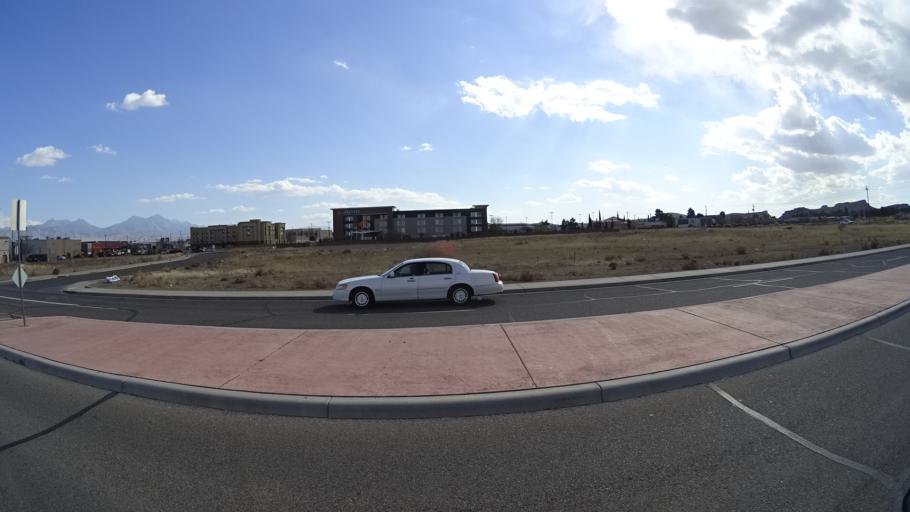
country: US
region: Arizona
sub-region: Mohave County
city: Kingman
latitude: 35.2252
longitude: -114.0388
